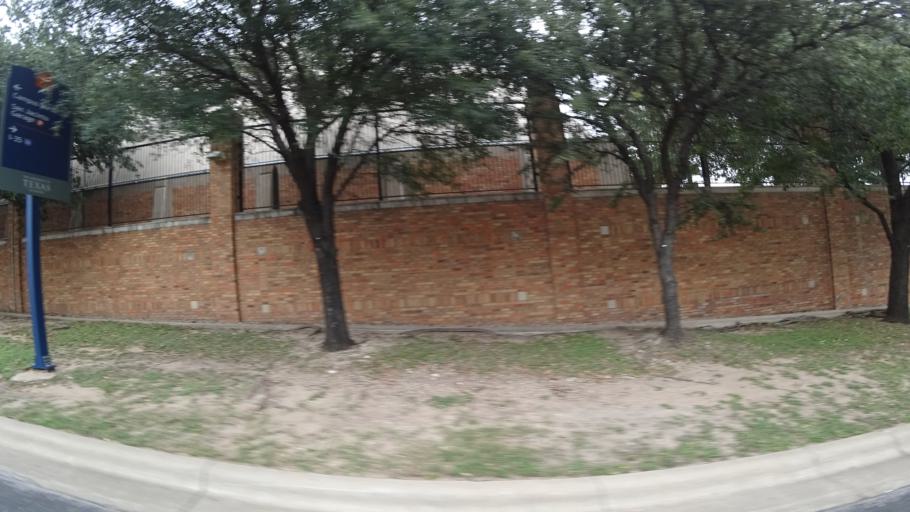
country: US
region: Texas
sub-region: Travis County
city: Austin
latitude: 30.2858
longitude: -97.7271
